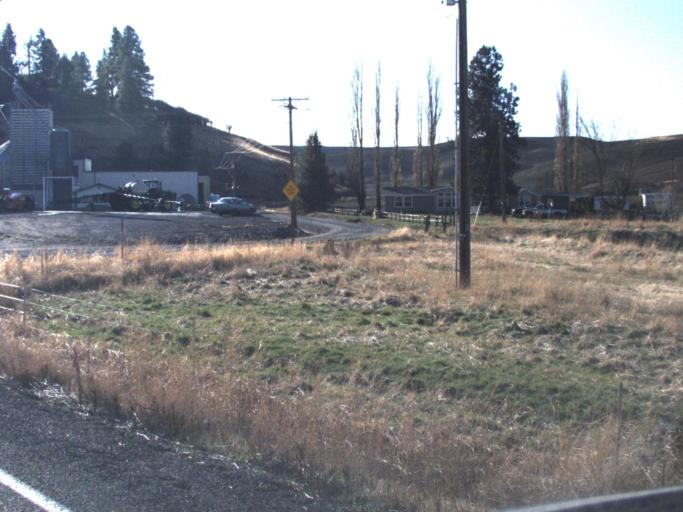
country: US
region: Washington
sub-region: Whitman County
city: Pullman
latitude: 46.7318
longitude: -117.3176
